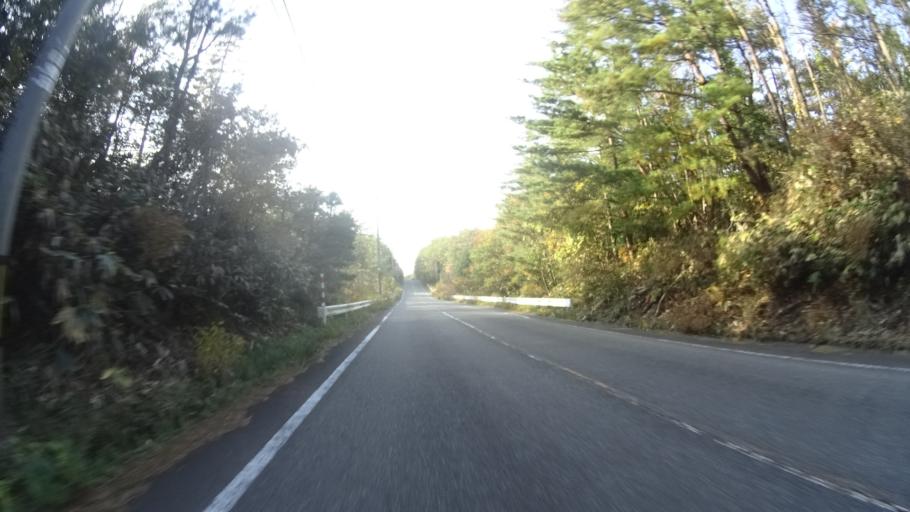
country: JP
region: Ishikawa
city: Hakui
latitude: 37.0690
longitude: 136.7492
